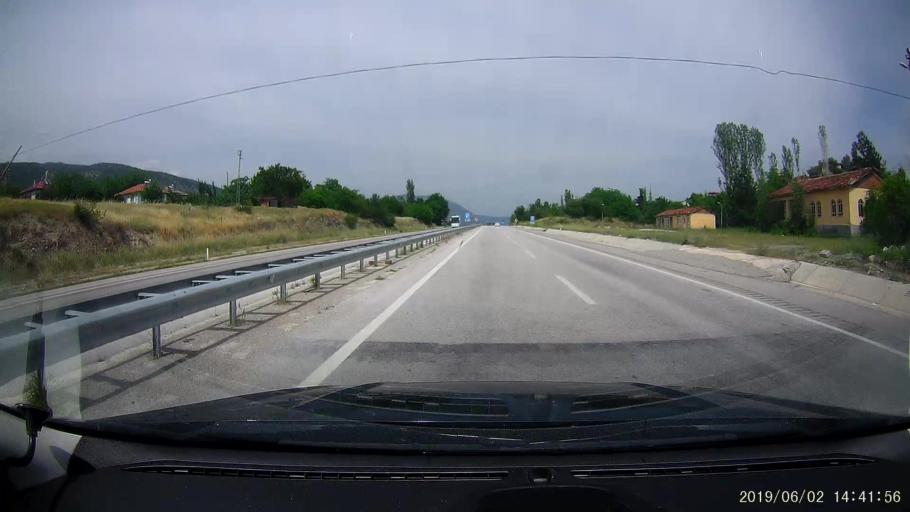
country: TR
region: Corum
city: Hacihamza
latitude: 41.0942
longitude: 34.3491
